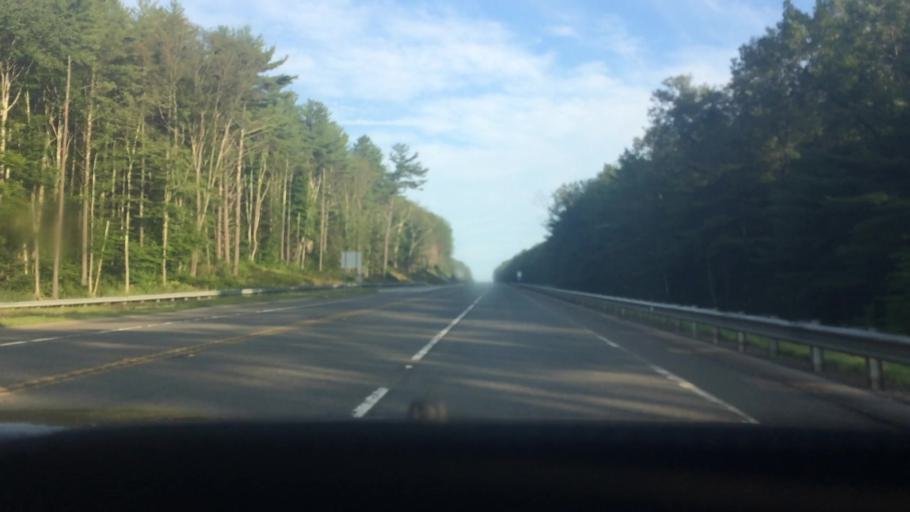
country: US
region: Massachusetts
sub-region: Franklin County
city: Orange
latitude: 42.5599
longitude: -72.3040
